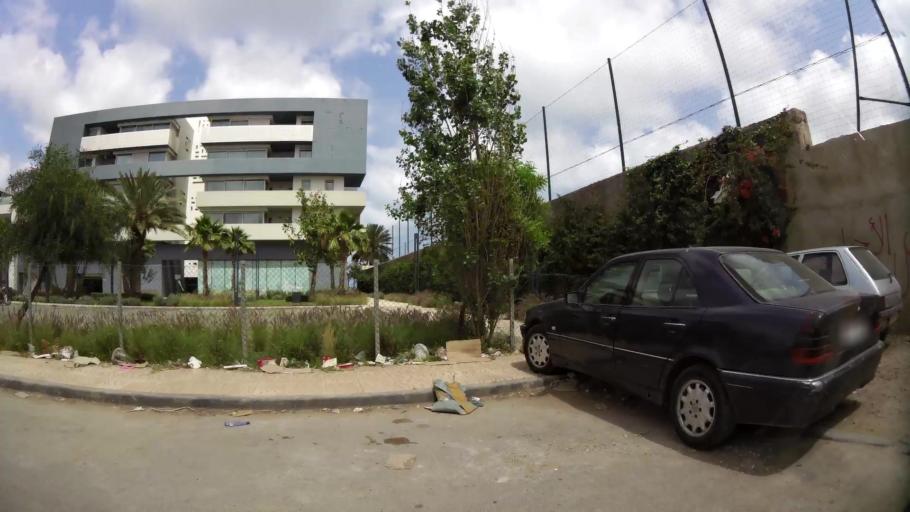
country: MA
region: Oriental
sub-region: Nador
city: Nador
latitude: 35.1773
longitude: -2.9221
